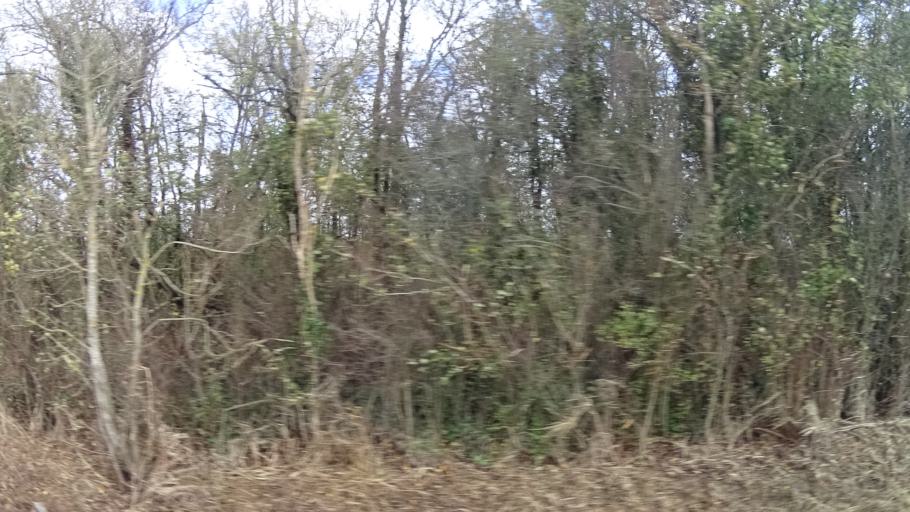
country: FR
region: Brittany
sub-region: Departement du Morbihan
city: Rieux
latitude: 47.5896
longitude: -2.0857
